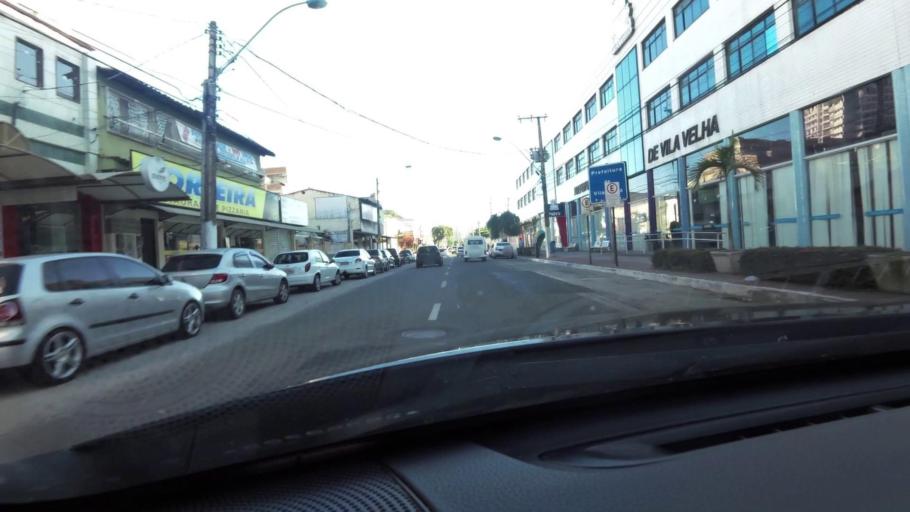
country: BR
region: Espirito Santo
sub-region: Vila Velha
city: Vila Velha
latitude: -20.3597
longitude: -40.2987
